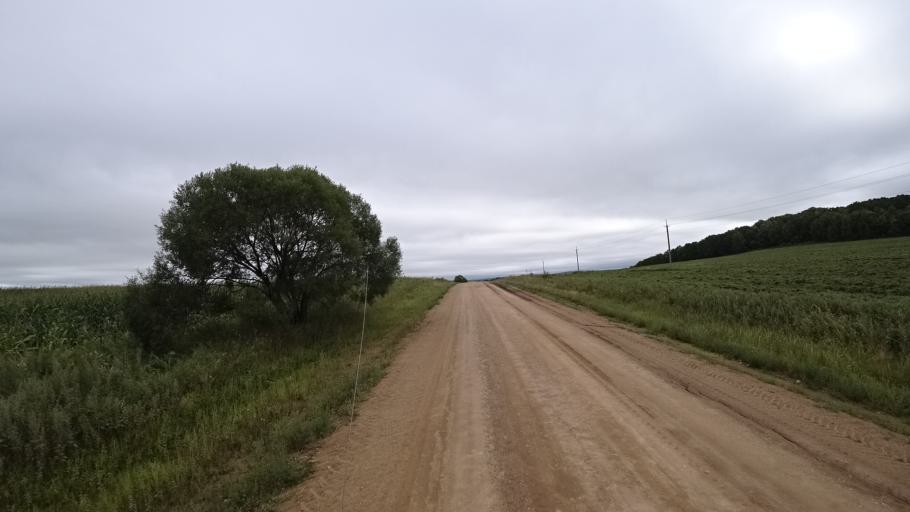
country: RU
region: Primorskiy
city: Monastyrishche
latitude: 44.0920
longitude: 132.5992
